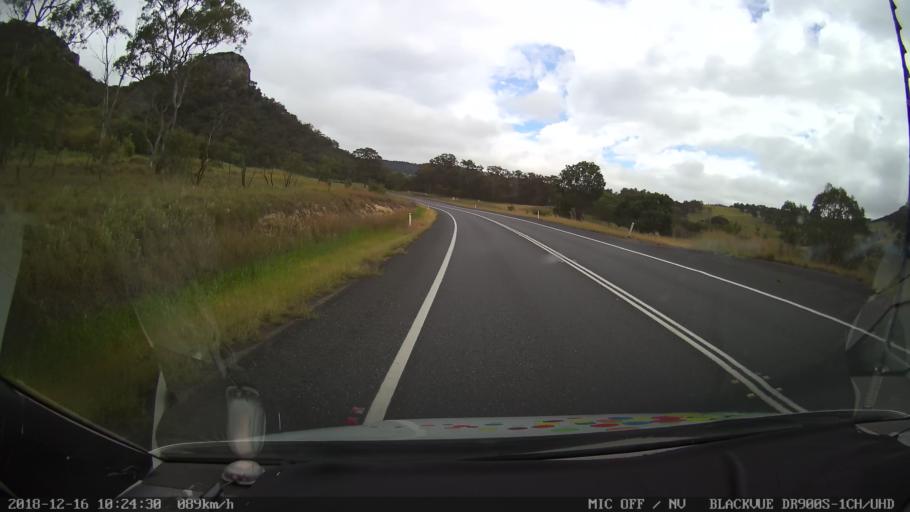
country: AU
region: New South Wales
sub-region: Tenterfield Municipality
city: Carrolls Creek
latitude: -29.1696
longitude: 152.0066
